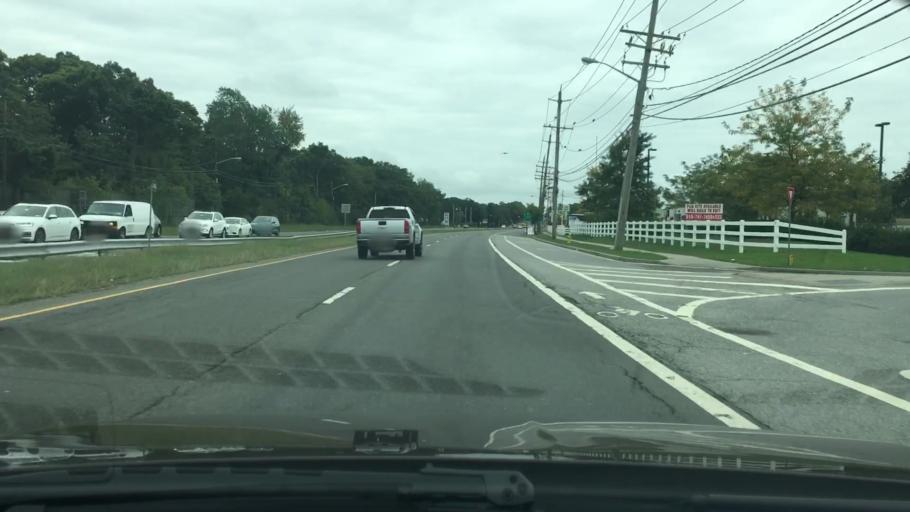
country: US
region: New York
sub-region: Suffolk County
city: Islandia
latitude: 40.8022
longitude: -73.1763
